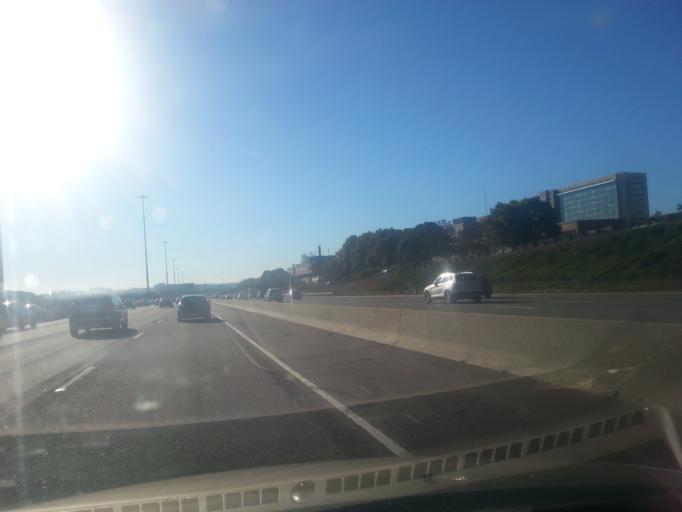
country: CA
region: Ontario
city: Toronto
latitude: 43.7227
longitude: -79.4817
